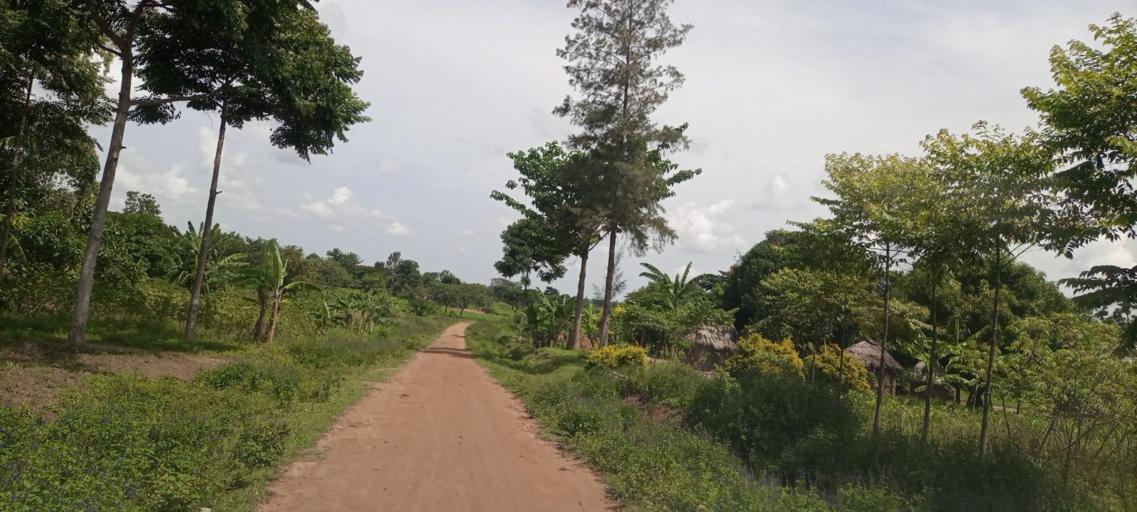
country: UG
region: Eastern Region
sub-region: Budaka District
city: Budaka
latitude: 1.1772
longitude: 33.9216
